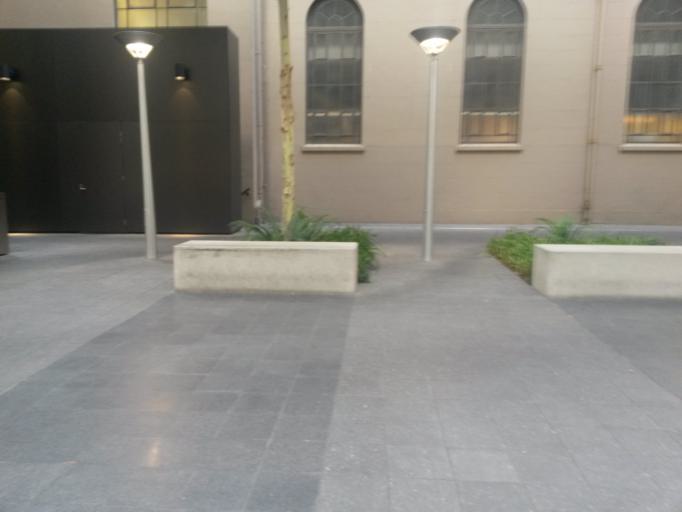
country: AU
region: South Australia
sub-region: Adelaide
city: Adelaide
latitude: -34.9247
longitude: 138.5991
